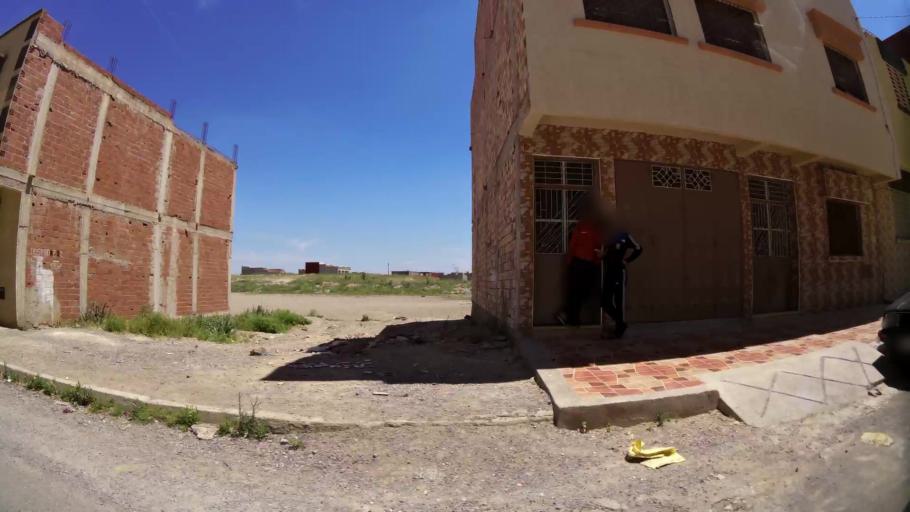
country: MA
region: Oriental
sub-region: Oujda-Angad
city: Oujda
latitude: 34.6556
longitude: -1.9476
